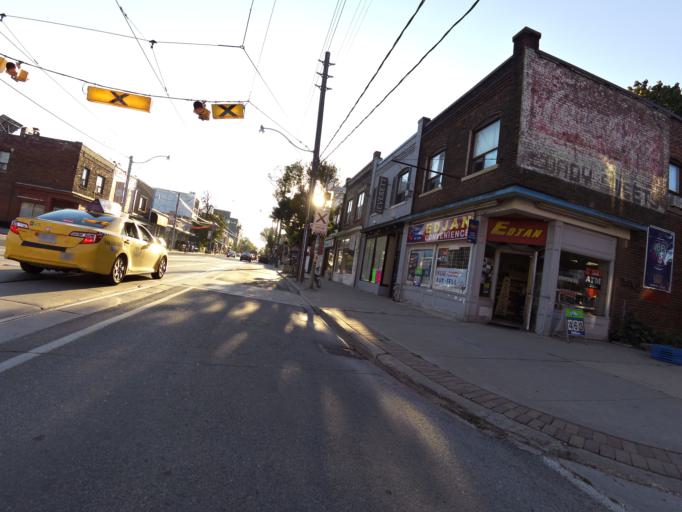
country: CA
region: Ontario
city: Toronto
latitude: 43.6624
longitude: -79.3341
